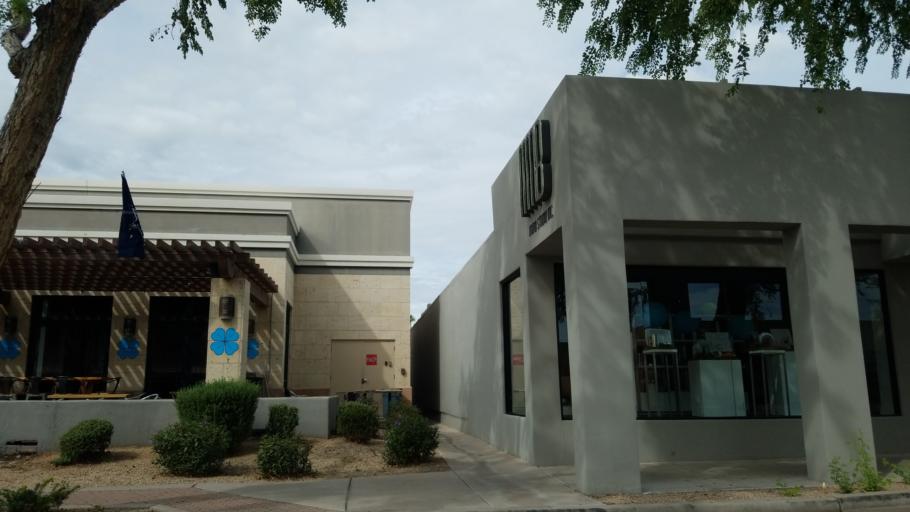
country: US
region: Arizona
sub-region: Maricopa County
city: Scottsdale
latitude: 33.4954
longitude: -111.9290
